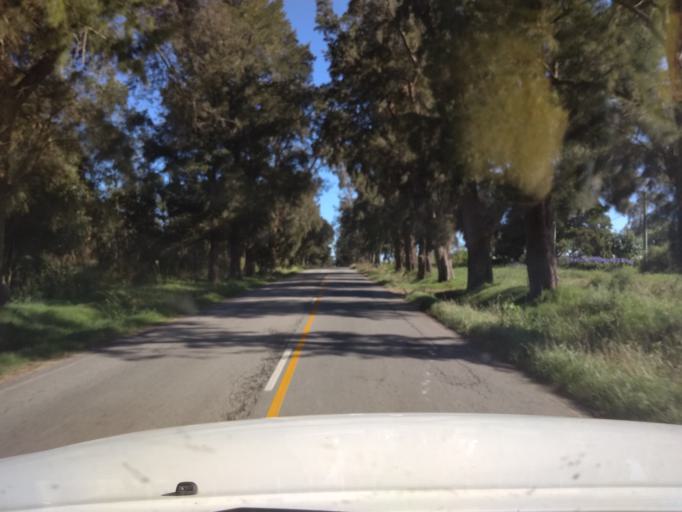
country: UY
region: Canelones
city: San Bautista
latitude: -34.3722
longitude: -55.9595
